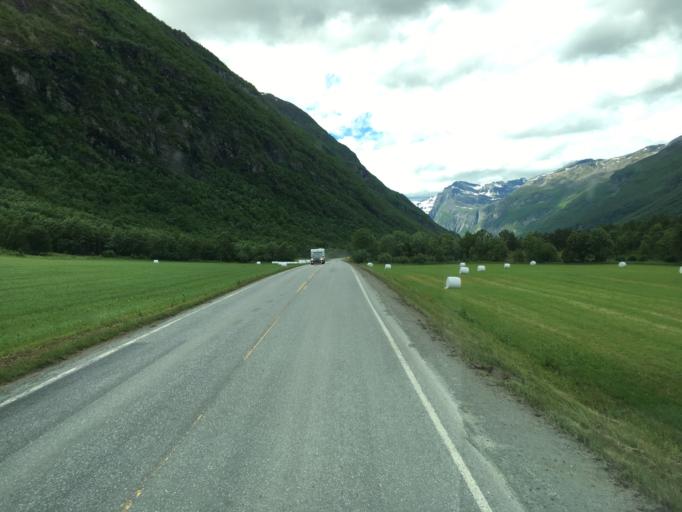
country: NO
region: More og Romsdal
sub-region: Sunndal
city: Sunndalsora
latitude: 62.5950
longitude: 8.9562
